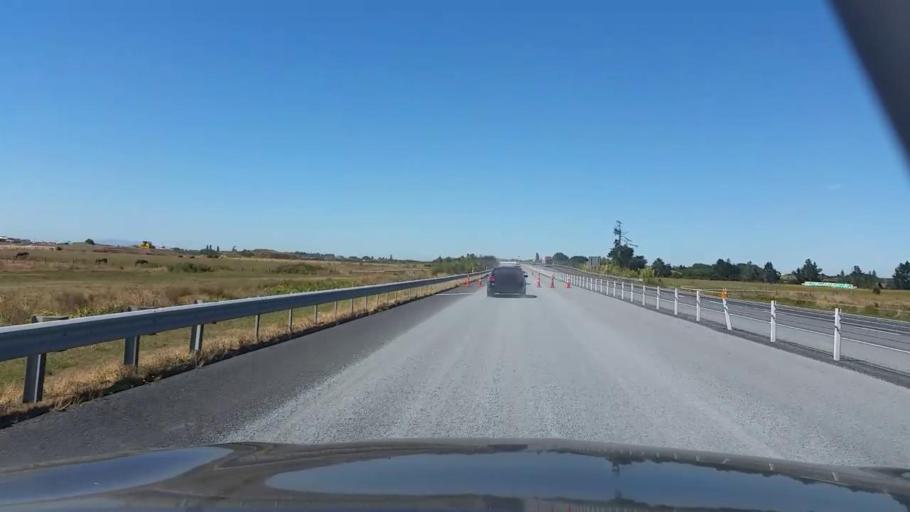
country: NZ
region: Waikato
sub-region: Hamilton City
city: Hamilton
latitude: -37.7440
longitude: 175.2142
